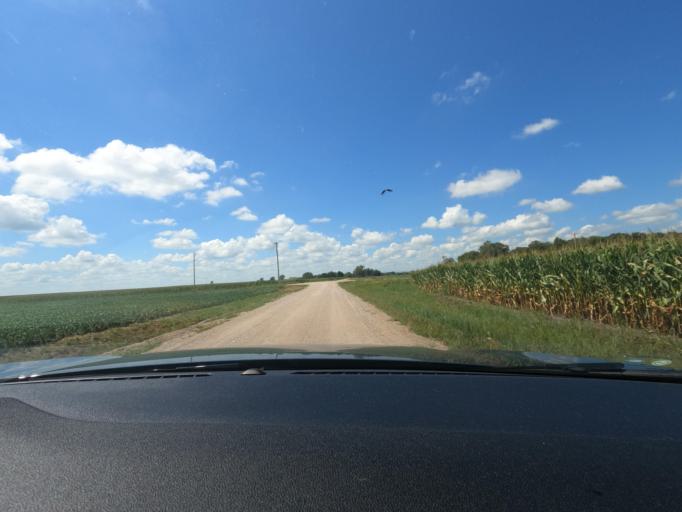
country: US
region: Nebraska
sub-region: Saunders County
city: Wahoo
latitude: 41.2492
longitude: -96.5626
